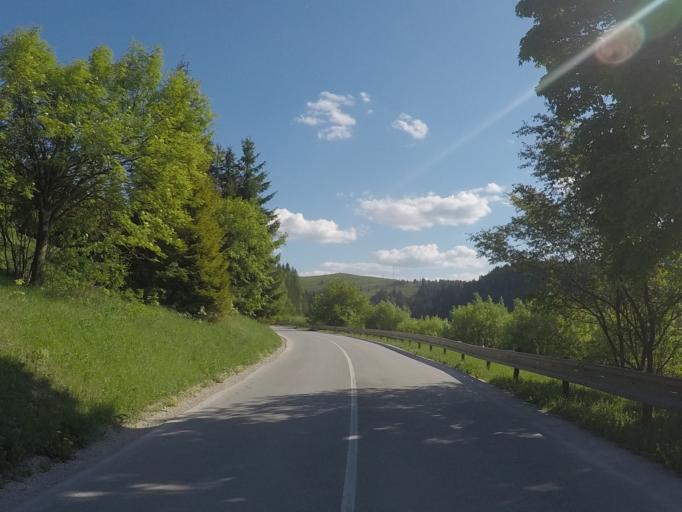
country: SK
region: Kosicky
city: Dobsina
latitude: 48.8615
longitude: 20.3854
